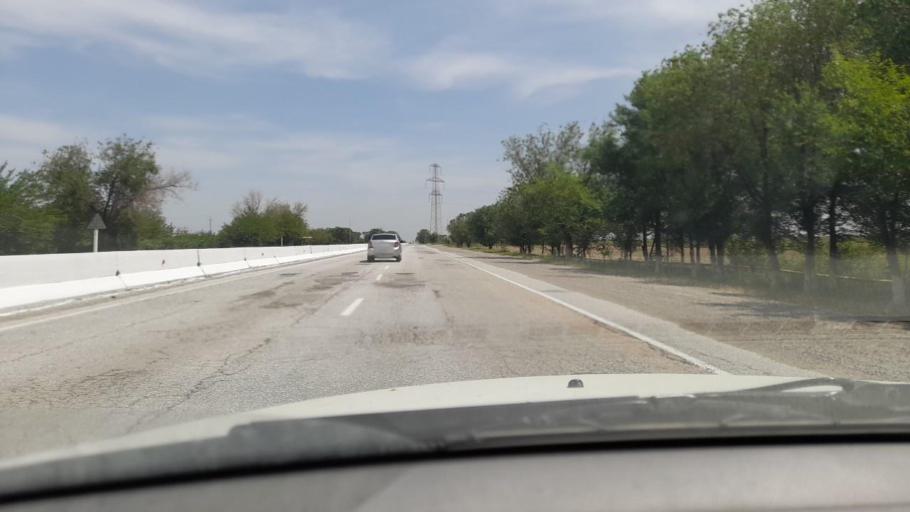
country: UZ
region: Navoiy
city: Konimex
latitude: 40.1138
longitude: 65.0913
